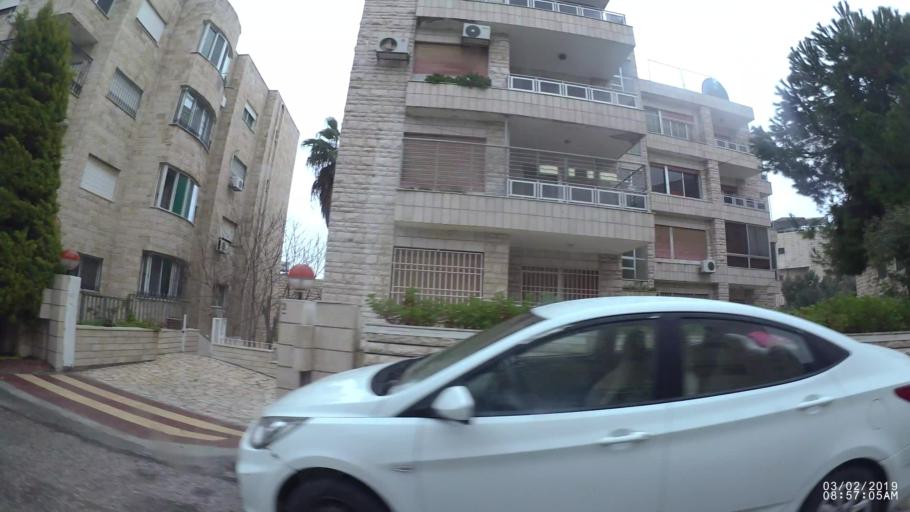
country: JO
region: Amman
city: Wadi as Sir
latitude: 31.9657
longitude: 35.8794
